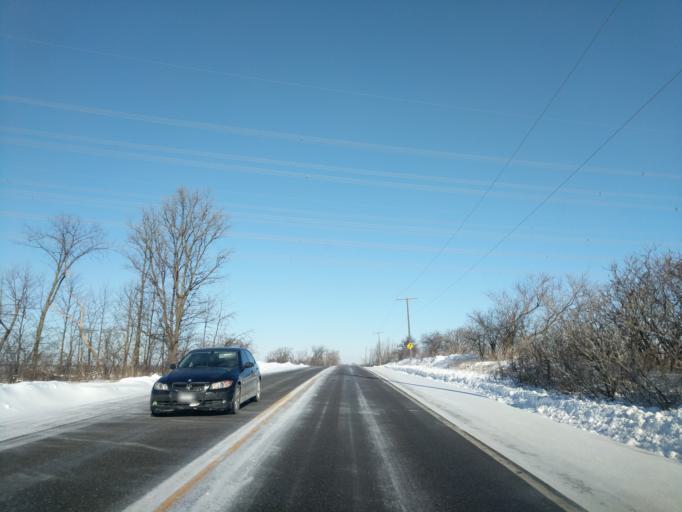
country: CA
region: Ontario
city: Pickering
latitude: 43.8515
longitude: -79.1300
